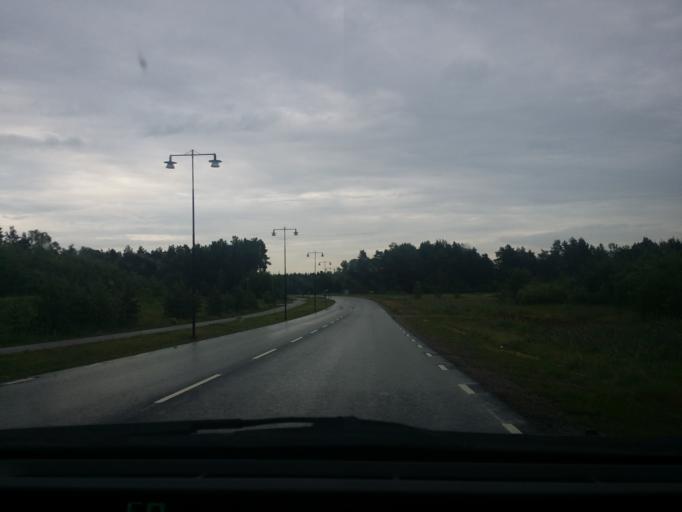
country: SE
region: Vaestmanland
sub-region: Arboga Kommun
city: Arboga
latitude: 59.4078
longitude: 15.8327
